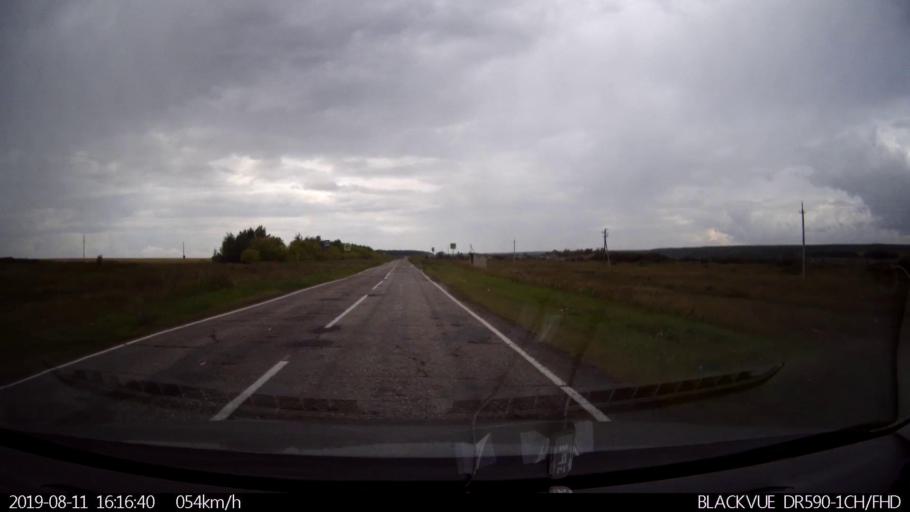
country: RU
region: Ulyanovsk
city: Mayna
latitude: 54.0428
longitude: 47.6202
